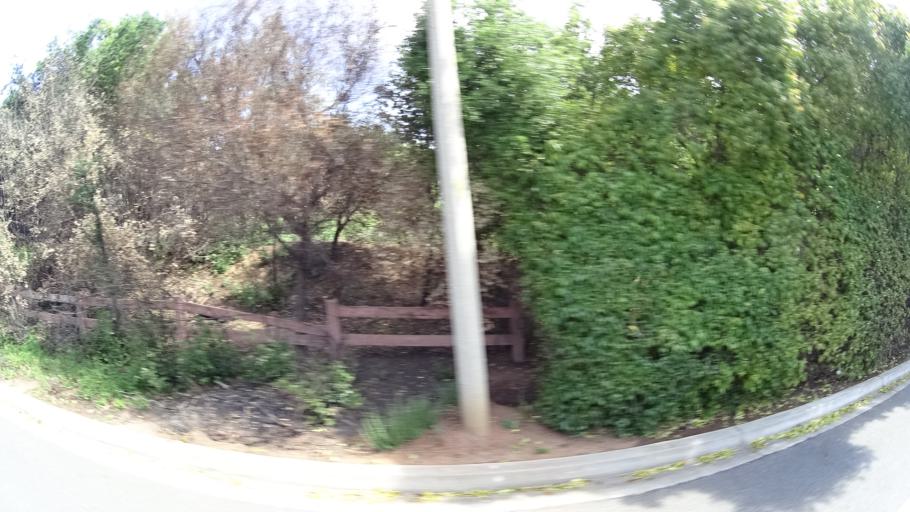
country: US
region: California
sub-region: Ventura County
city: Oak Park
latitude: 34.1927
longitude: -118.7997
